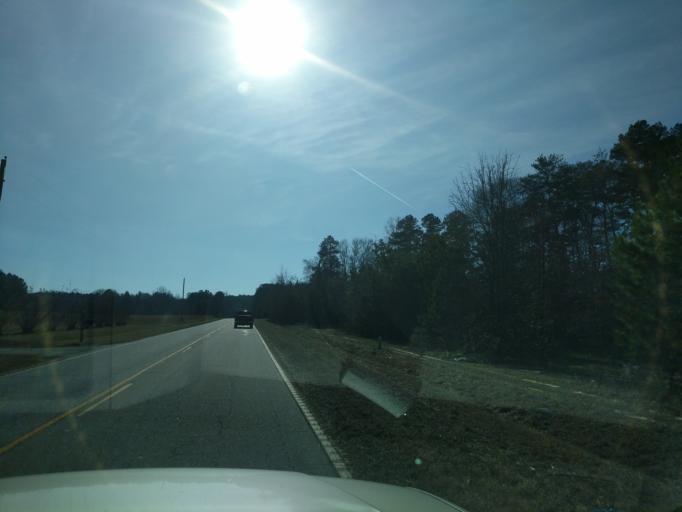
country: US
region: South Carolina
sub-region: Laurens County
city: Watts Mills
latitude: 34.6101
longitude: -81.9832
